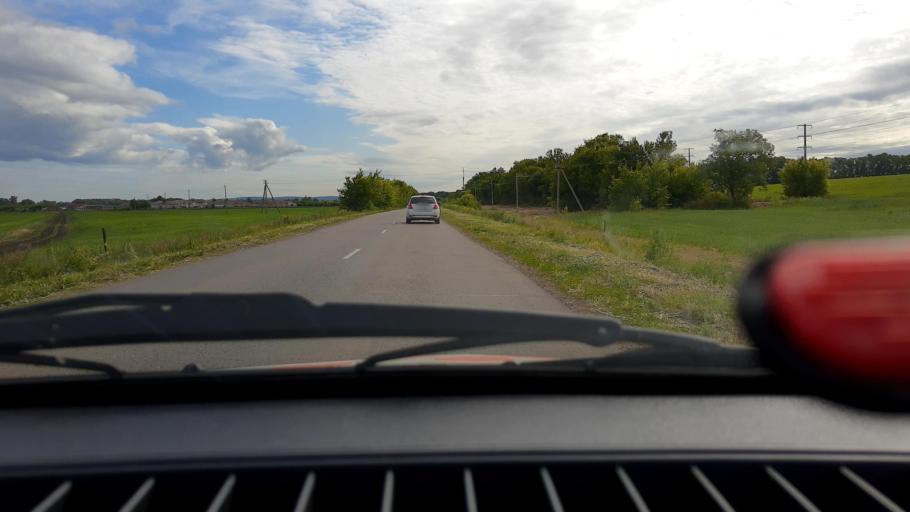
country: RU
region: Bashkortostan
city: Kabakovo
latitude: 54.5067
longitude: 55.9297
